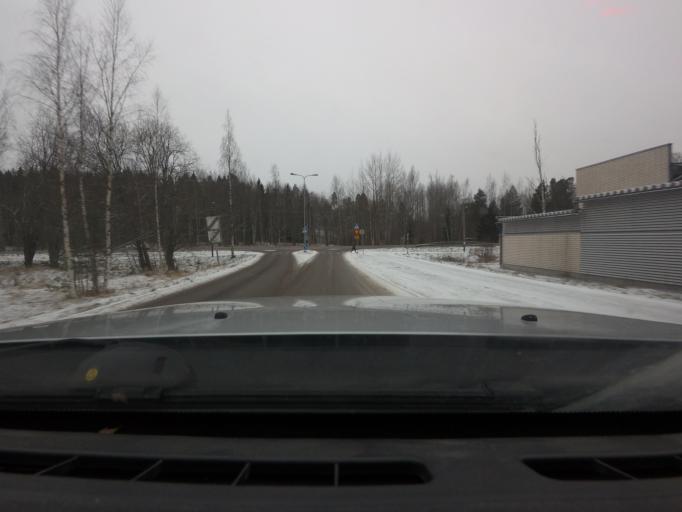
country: FI
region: Uusimaa
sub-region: Helsinki
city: Kauniainen
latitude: 60.2248
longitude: 24.7267
